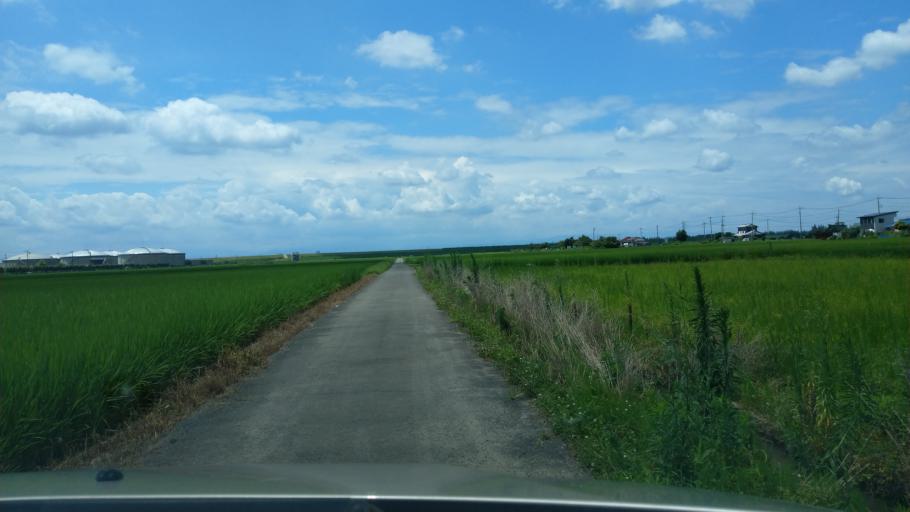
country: JP
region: Saitama
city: Yono
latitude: 35.8812
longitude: 139.5941
